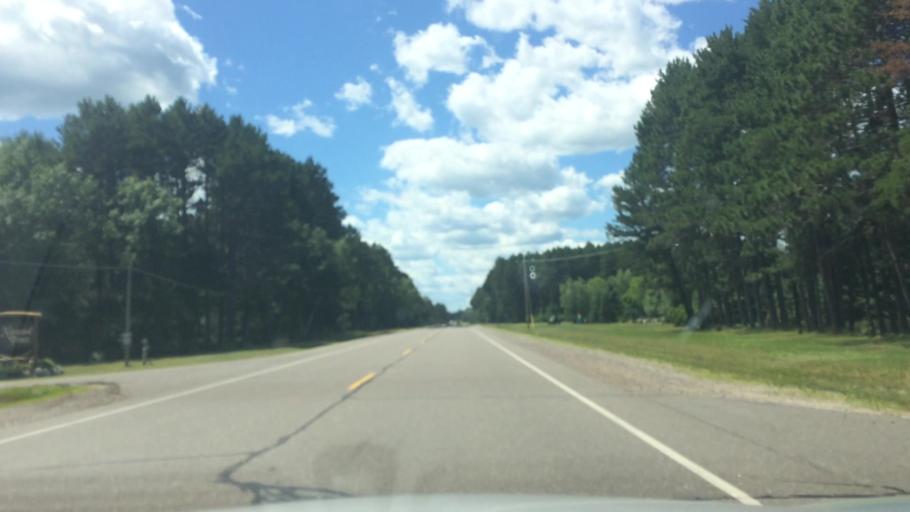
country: US
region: Wisconsin
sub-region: Vilas County
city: Lac du Flambeau
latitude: 45.8833
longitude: -89.7473
